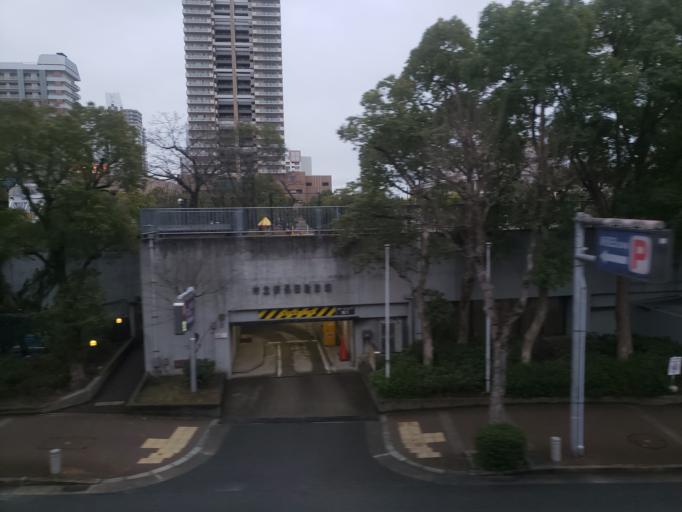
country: JP
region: Hyogo
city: Kobe
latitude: 34.6563
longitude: 135.1432
